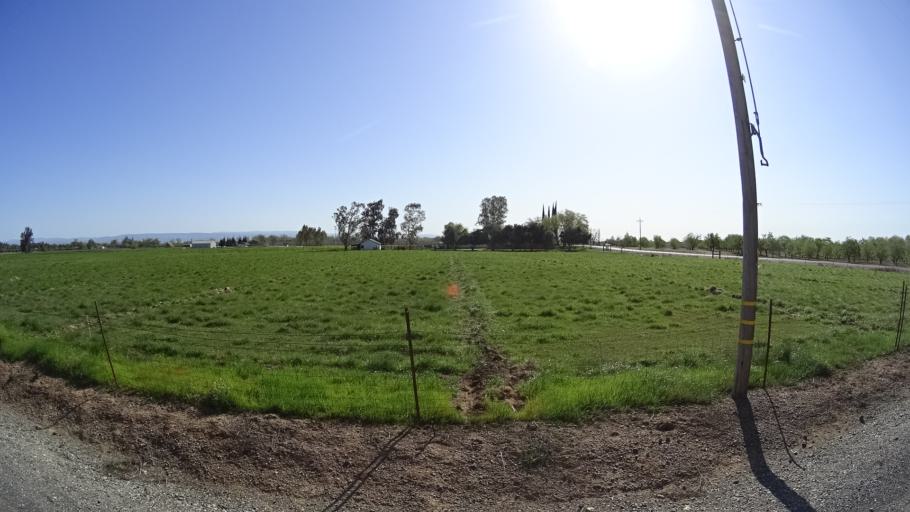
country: US
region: California
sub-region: Glenn County
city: Hamilton City
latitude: 39.7902
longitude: -122.0669
